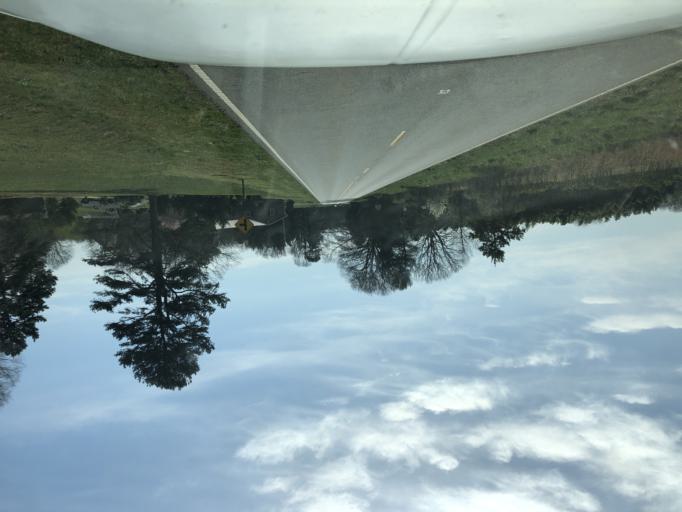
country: US
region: North Carolina
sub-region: Cleveland County
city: Shelby
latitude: 35.3844
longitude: -81.6206
